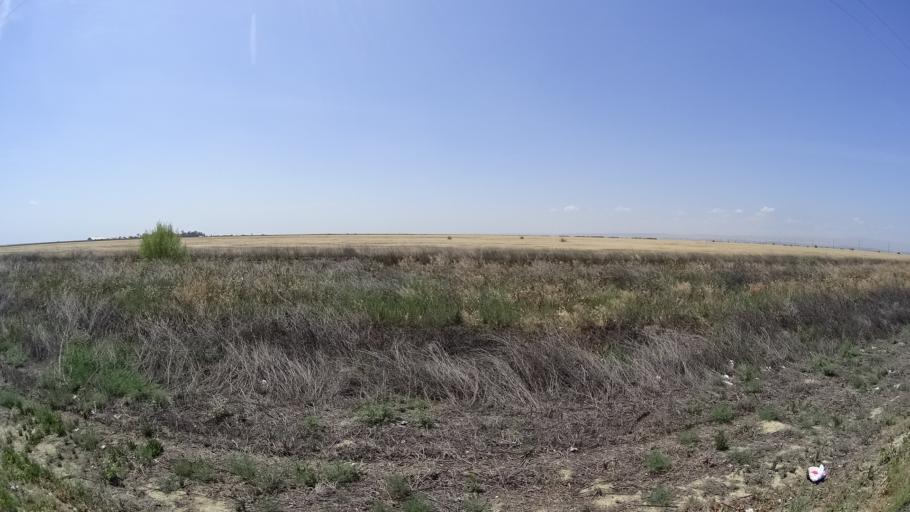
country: US
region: California
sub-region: Kings County
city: Stratford
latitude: 36.1378
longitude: -119.8999
